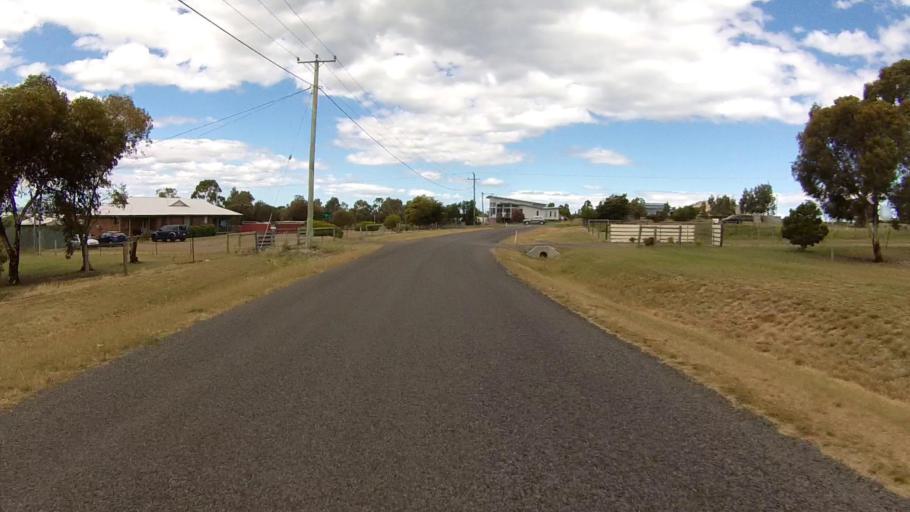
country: AU
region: Tasmania
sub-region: Clarence
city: Cambridge
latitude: -42.8498
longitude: 147.4745
